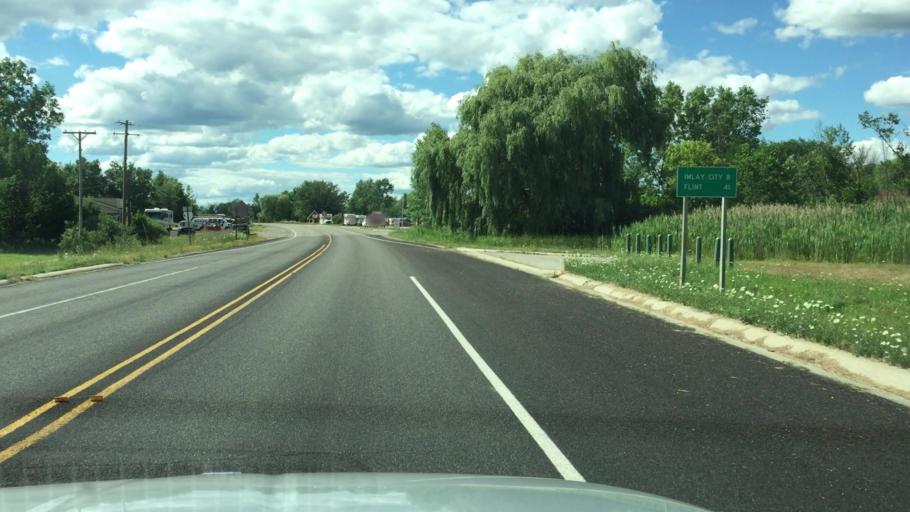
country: US
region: Michigan
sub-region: Saint Clair County
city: Capac
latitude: 43.0231
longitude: -82.9294
